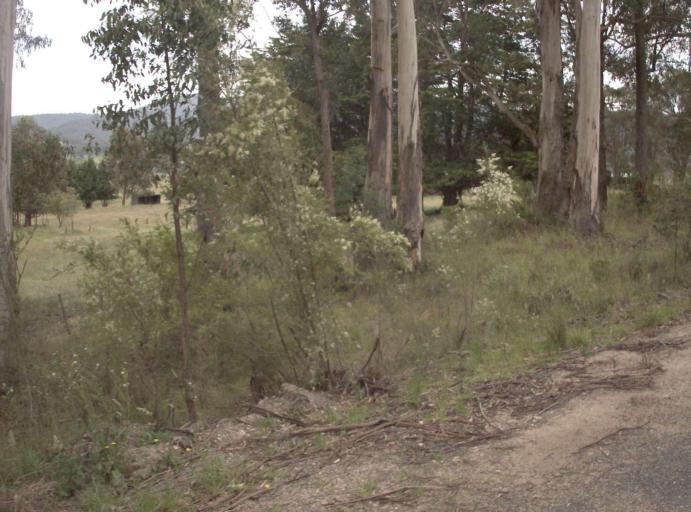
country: AU
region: New South Wales
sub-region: Bombala
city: Bombala
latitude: -37.4952
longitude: 149.1812
